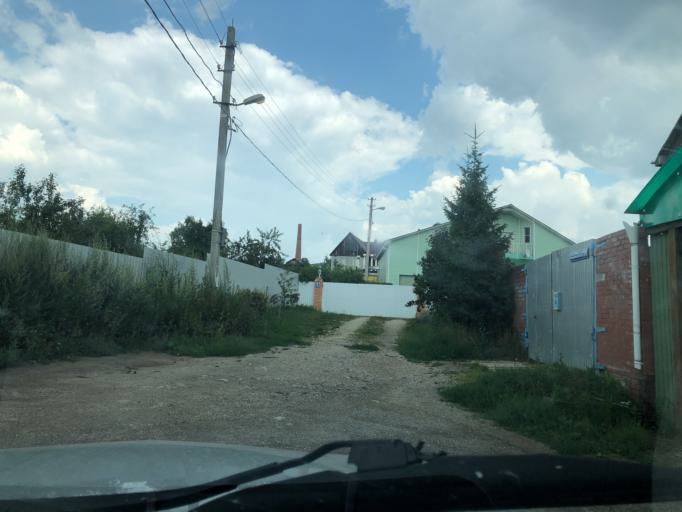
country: RU
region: Tula
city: Mendeleyevskiy
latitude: 54.1590
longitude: 37.5651
